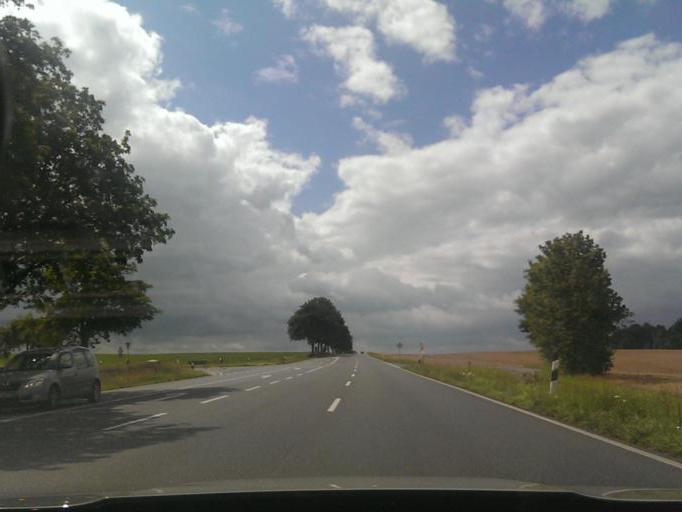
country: DE
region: Lower Saxony
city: Holenberg
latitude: 51.9118
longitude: 9.6109
